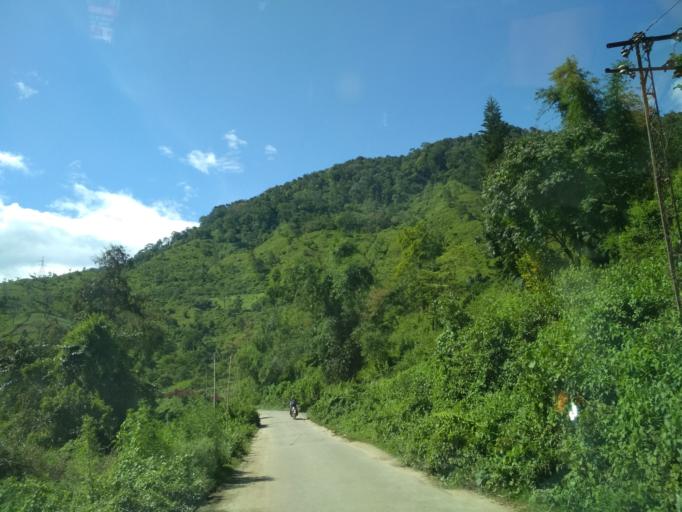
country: IN
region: Arunachal Pradesh
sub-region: Lower Subansiri
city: Ziro
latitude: 27.3615
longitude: 93.7788
